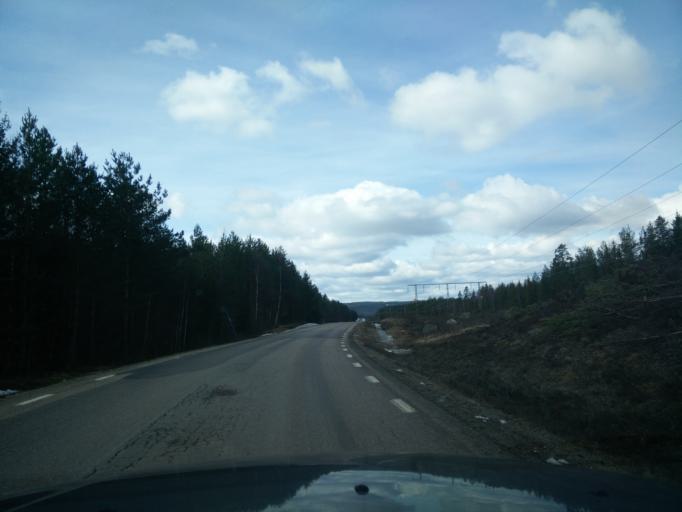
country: SE
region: Vaermland
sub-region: Hagfors Kommun
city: Hagfors
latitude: 60.0346
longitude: 13.5614
